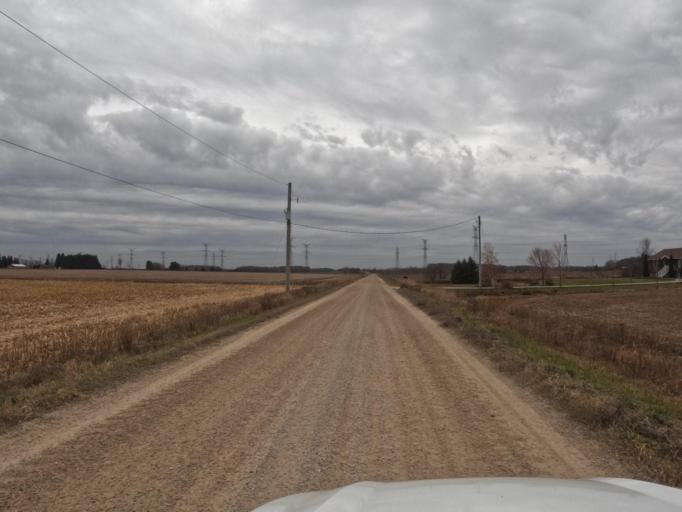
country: CA
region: Ontario
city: Shelburne
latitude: 43.9937
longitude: -80.3855
